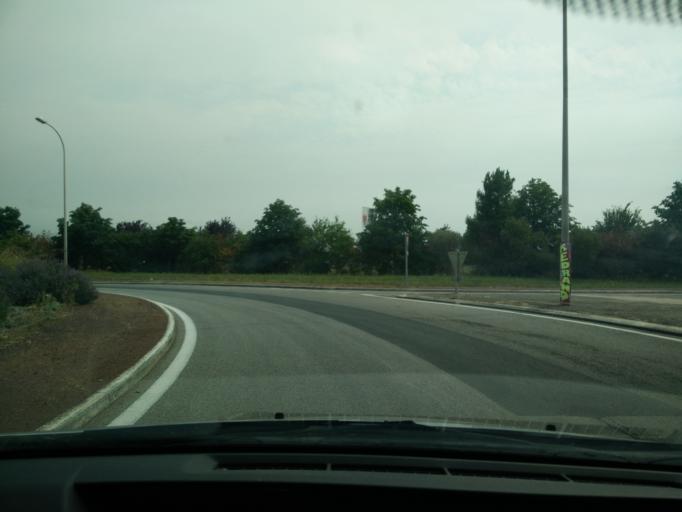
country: FR
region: Poitou-Charentes
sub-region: Departement des Deux-Sevres
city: Sainte-Verge
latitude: 46.9899
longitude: -0.1963
